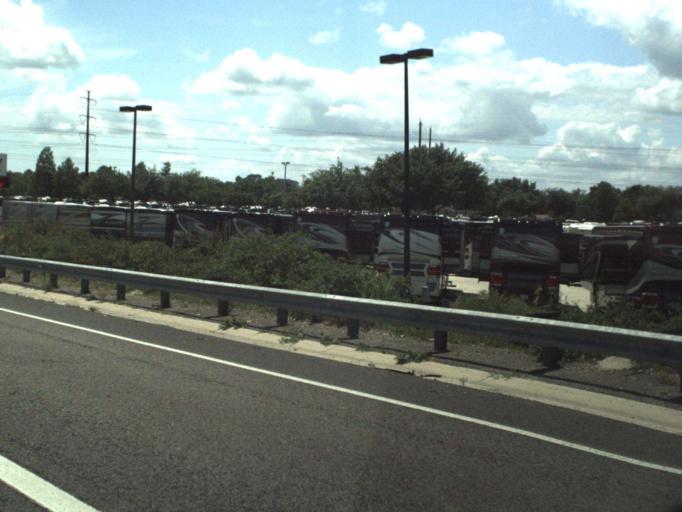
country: US
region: Florida
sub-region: Volusia County
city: DeBary
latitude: 28.8279
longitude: -81.3271
